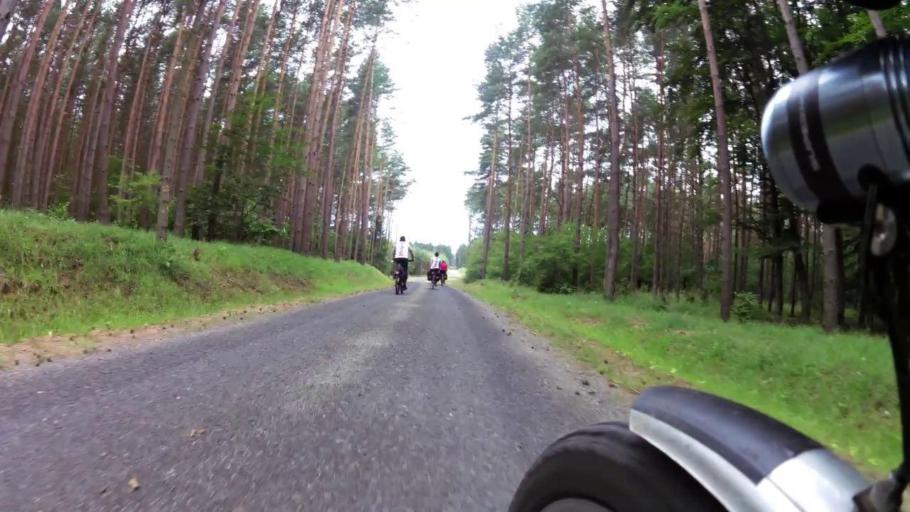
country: PL
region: West Pomeranian Voivodeship
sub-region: Powiat mysliborski
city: Boleszkowice
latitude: 52.8281
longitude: 14.6031
